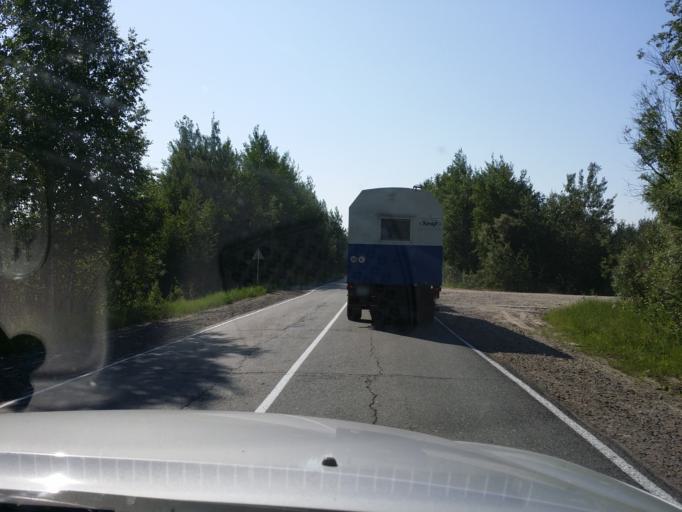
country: RU
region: Khanty-Mansiyskiy Avtonomnyy Okrug
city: Izluchinsk
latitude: 60.8521
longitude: 77.0723
